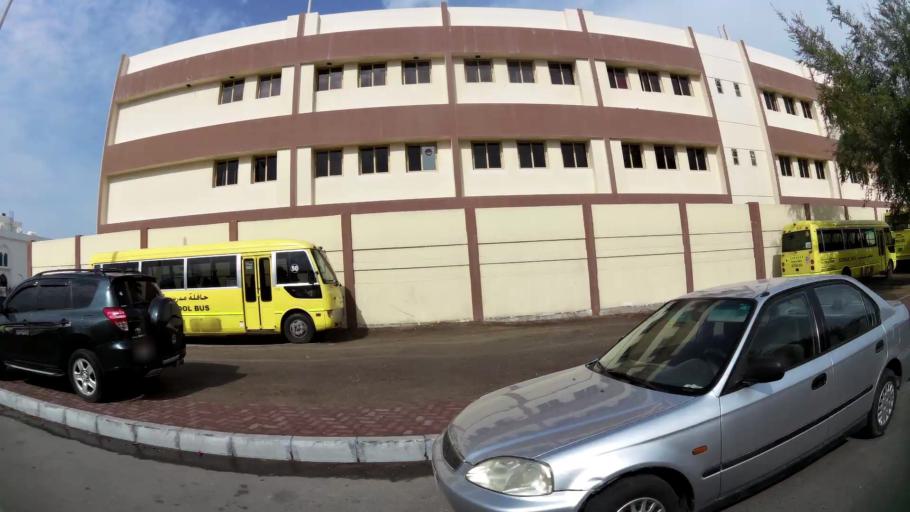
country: AE
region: Abu Dhabi
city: Abu Dhabi
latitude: 24.4441
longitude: 54.4113
